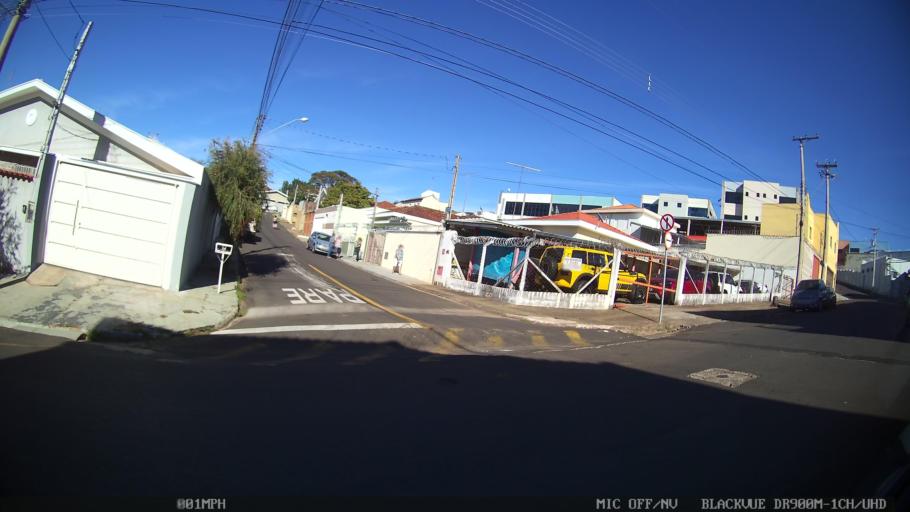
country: BR
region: Sao Paulo
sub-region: Franca
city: Franca
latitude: -20.5304
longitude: -47.4114
